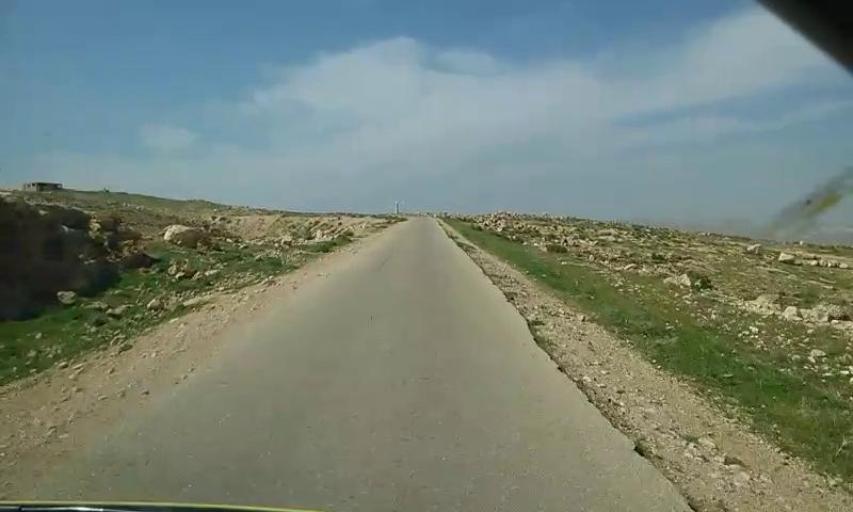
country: PS
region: West Bank
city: Khallat al Mayyah
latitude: 31.4404
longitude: 35.2052
